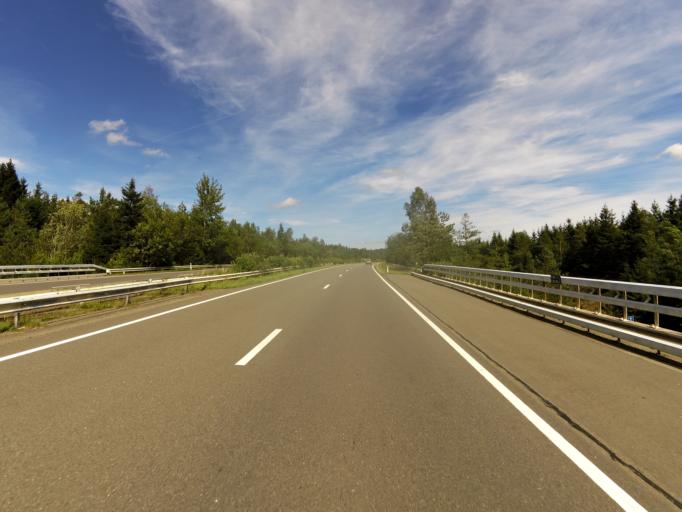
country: BE
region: Wallonia
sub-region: Province du Luxembourg
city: Saint-Hubert
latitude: 50.0484
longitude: 5.3957
